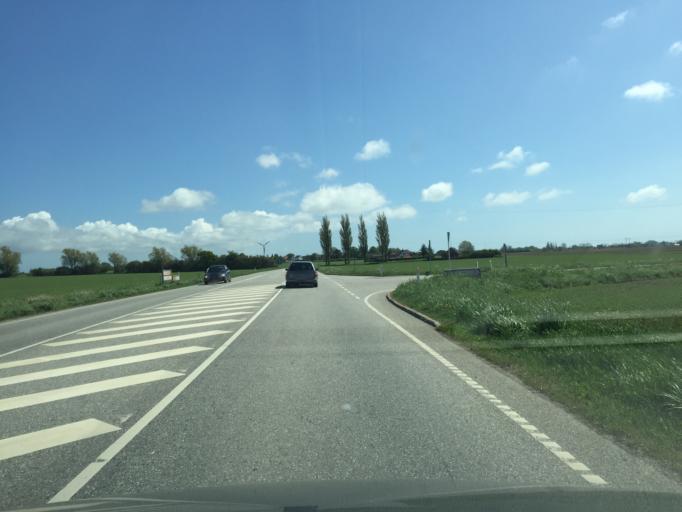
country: DK
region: Zealand
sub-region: Vordingborg Kommune
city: Stege
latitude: 54.9678
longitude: 12.2193
